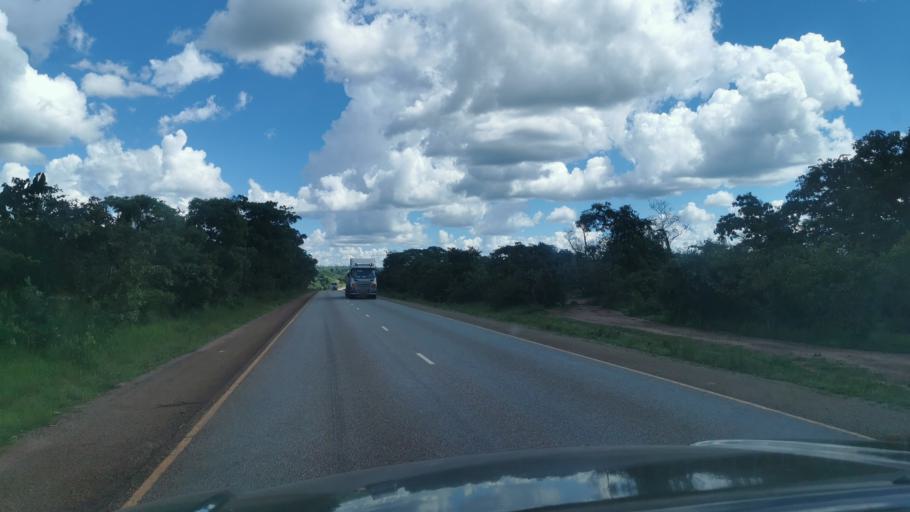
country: TZ
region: Geita
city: Uyovu
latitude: -3.0968
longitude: 31.3019
